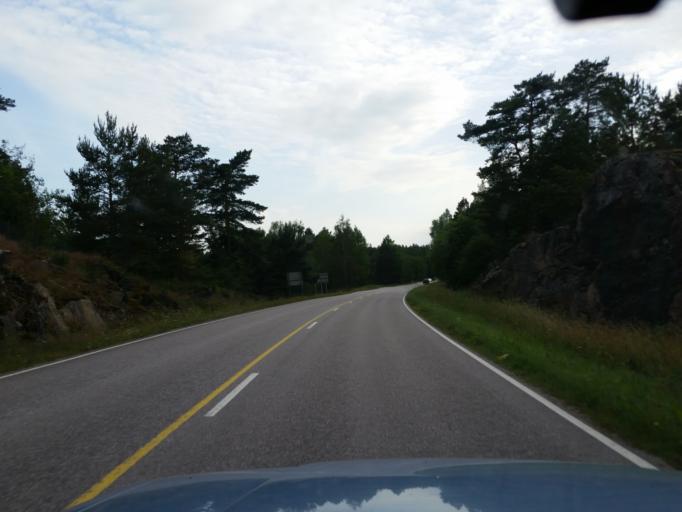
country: FI
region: Varsinais-Suomi
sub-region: Aboland-Turunmaa
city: Nagu
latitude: 60.1798
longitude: 21.9718
